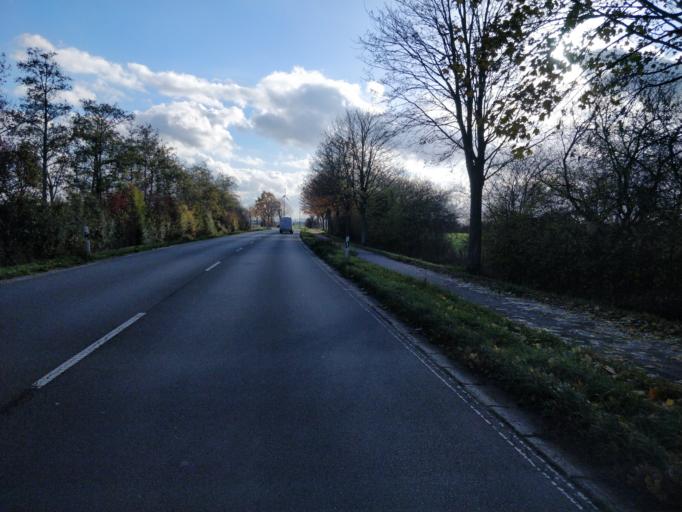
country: DE
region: North Rhine-Westphalia
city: Rees
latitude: 51.7884
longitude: 6.3740
